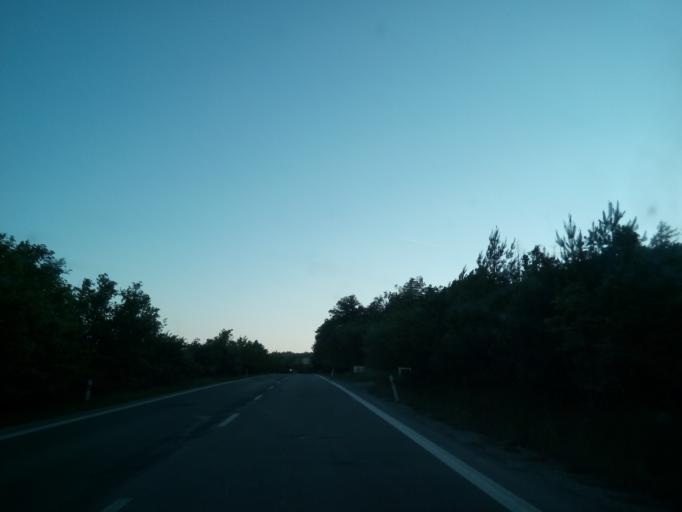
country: CZ
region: South Moravian
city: Bilovice nad Svitavou
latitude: 49.2263
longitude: 16.6918
